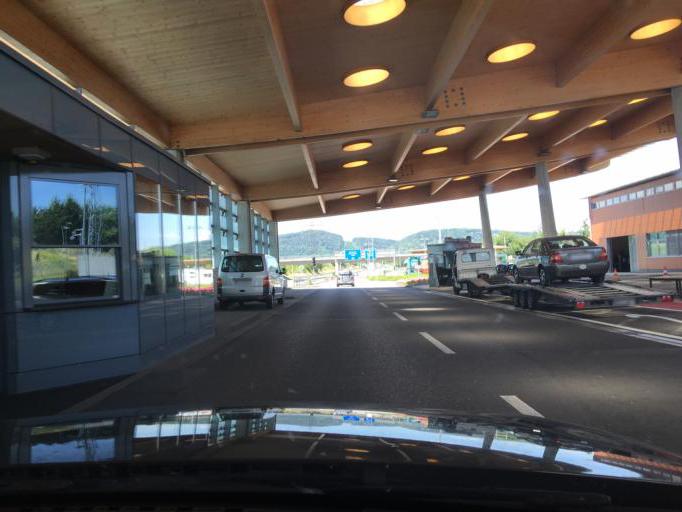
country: DE
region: Baden-Wuerttemberg
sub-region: Freiburg Region
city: Rheinfelden (Baden)
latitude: 47.5507
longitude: 7.7578
